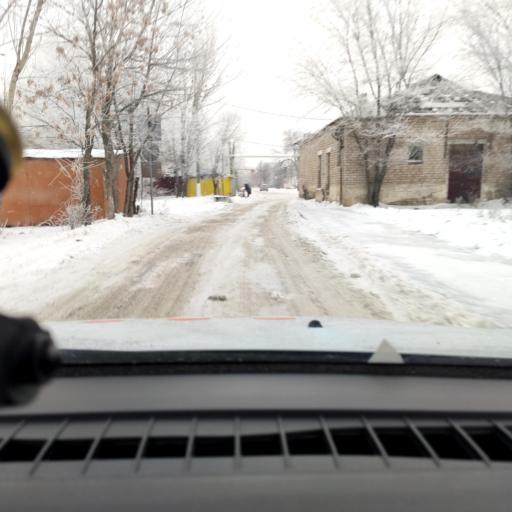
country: RU
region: Samara
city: Dubovyy Umet
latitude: 53.0784
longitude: 50.2293
